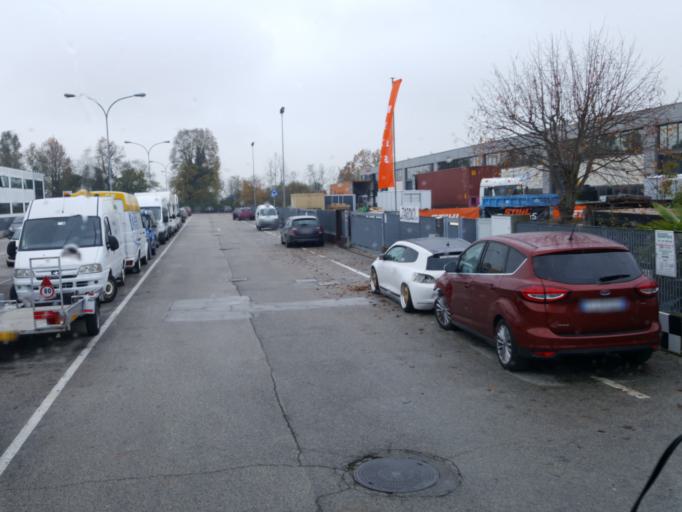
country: IT
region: Veneto
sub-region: Provincia di Treviso
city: Mogliano Veneto
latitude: 45.5523
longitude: 12.2266
